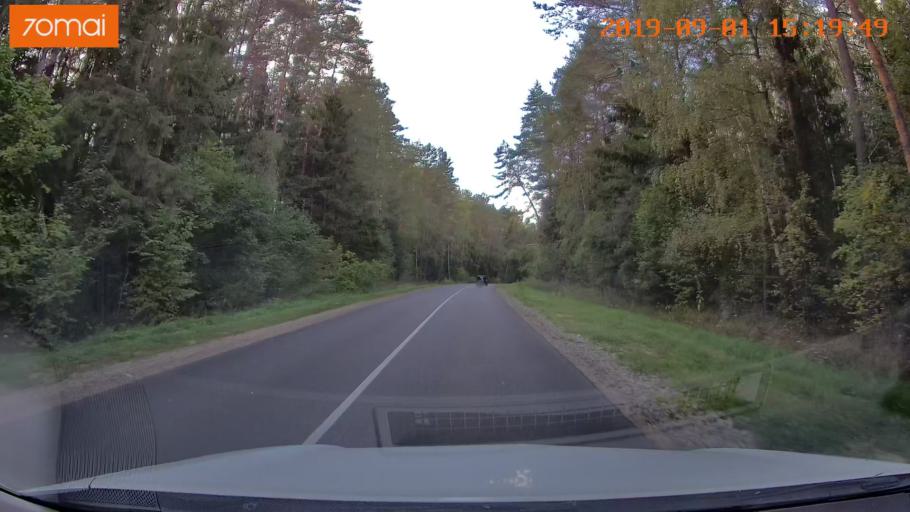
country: RU
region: Kaluga
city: Maloyaroslavets
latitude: 54.9143
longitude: 36.4868
